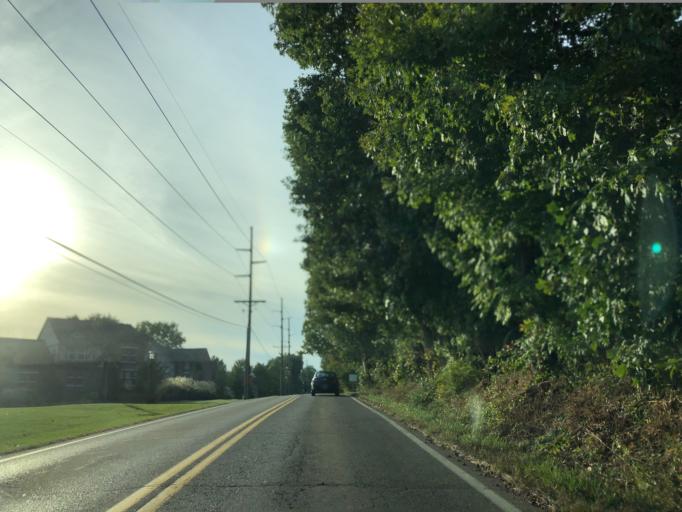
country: US
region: Ohio
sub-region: Warren County
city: Loveland Park
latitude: 39.2891
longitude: -84.2739
